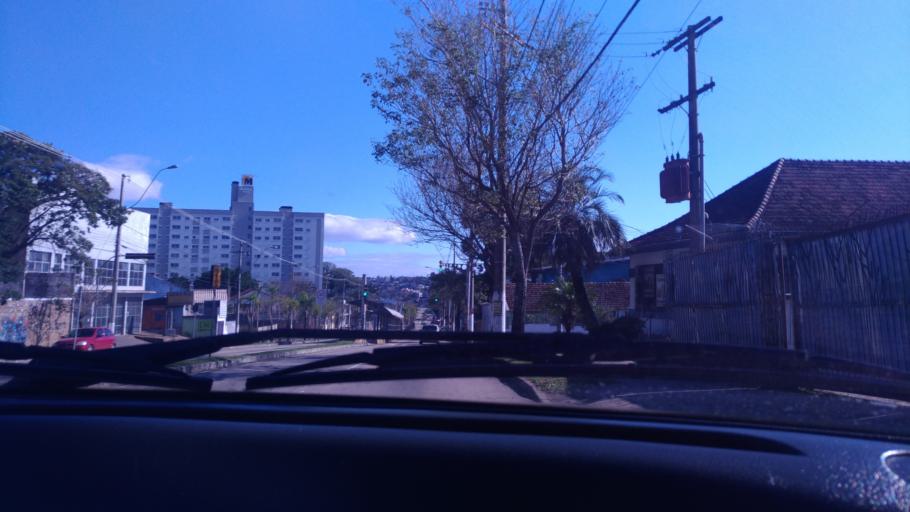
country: BR
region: Rio Grande do Sul
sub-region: Porto Alegre
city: Porto Alegre
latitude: -30.0724
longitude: -51.1946
